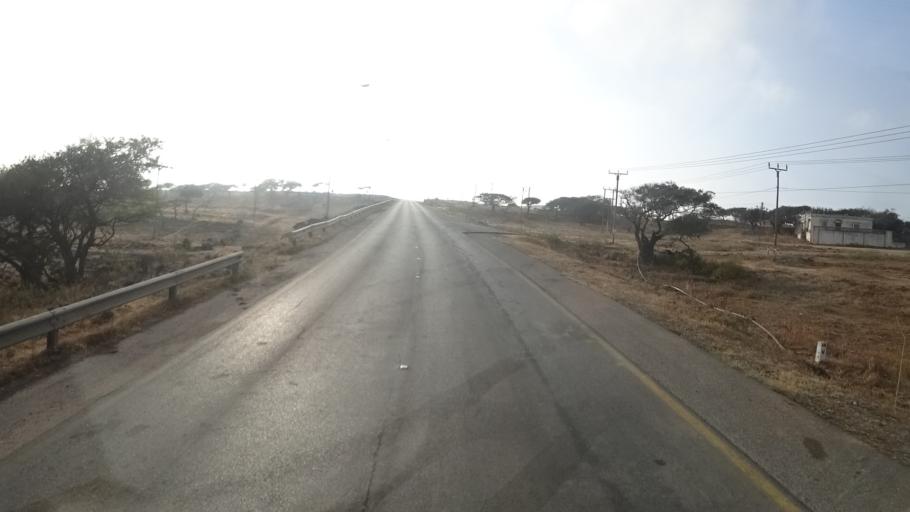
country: OM
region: Zufar
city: Salalah
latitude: 17.1200
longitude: 53.9830
